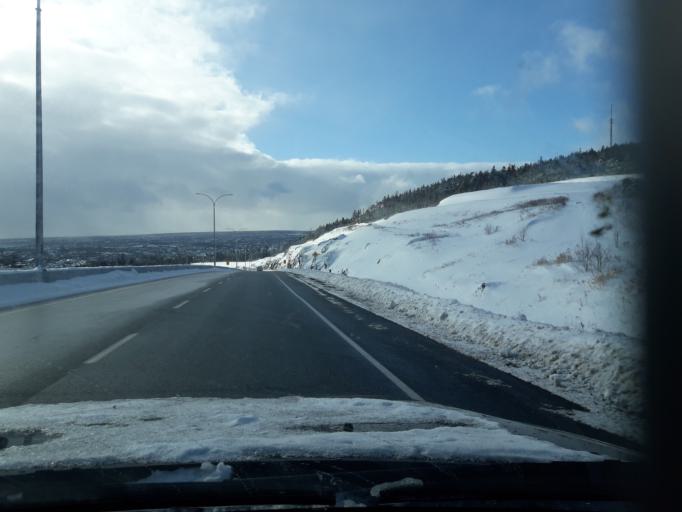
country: CA
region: Newfoundland and Labrador
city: Mount Pearl
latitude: 47.5352
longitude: -52.7771
